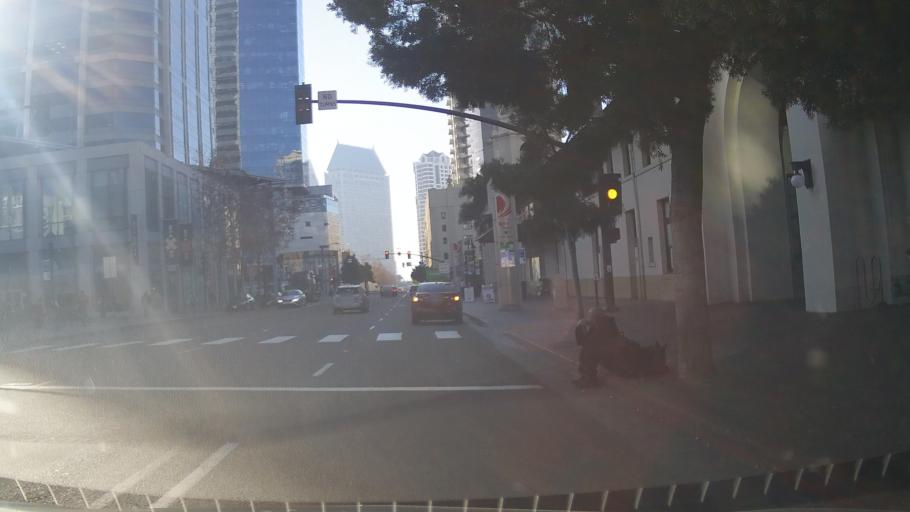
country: US
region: California
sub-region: San Diego County
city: San Diego
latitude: 32.7172
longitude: -117.1693
